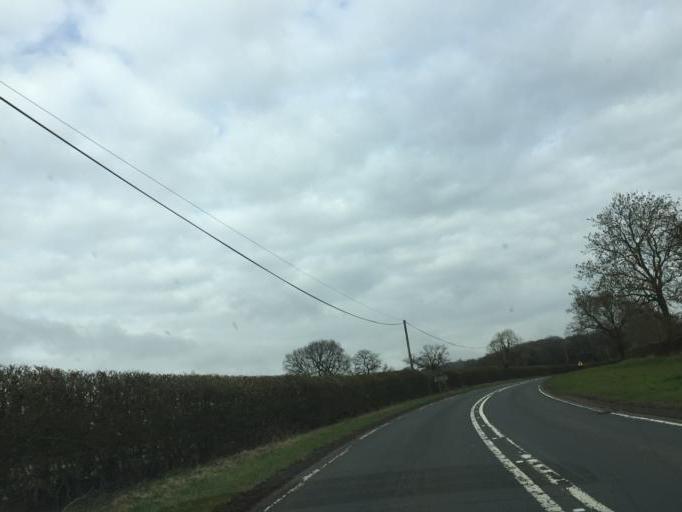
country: GB
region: England
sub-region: Warwickshire
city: Henley in Arden
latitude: 52.2940
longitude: -1.8276
